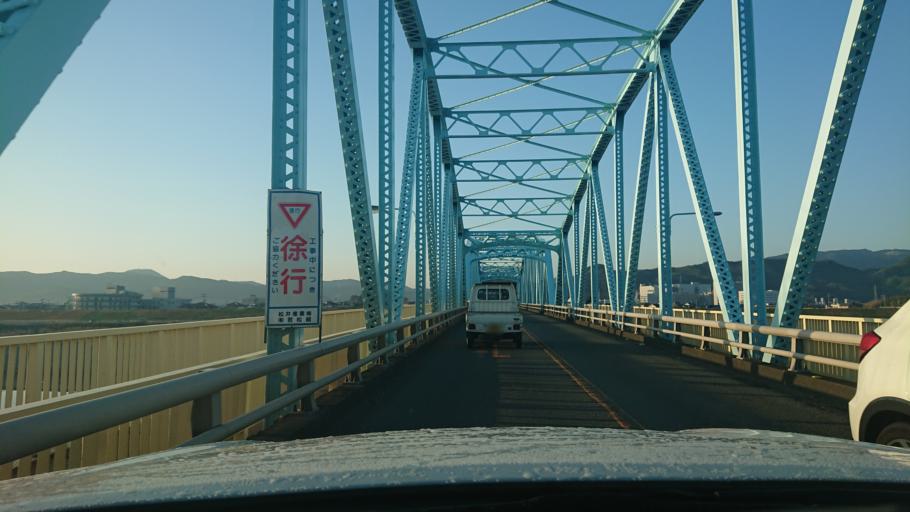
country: JP
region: Tokushima
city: Anan
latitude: 33.9400
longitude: 134.6216
